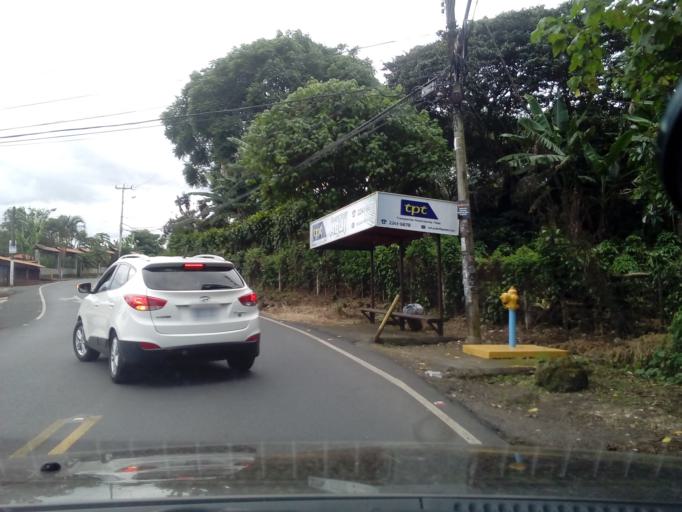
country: CR
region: Heredia
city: Mercedes
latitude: 10.0352
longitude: -84.1286
